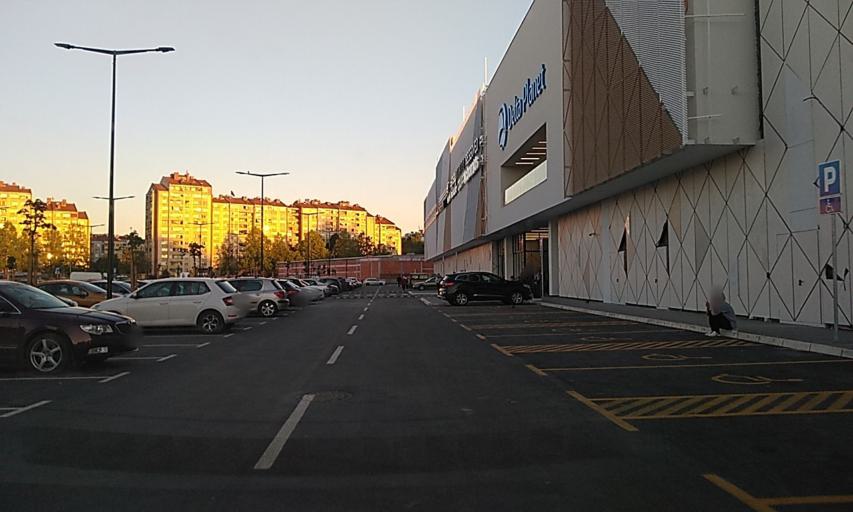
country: RS
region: Central Serbia
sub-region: Nisavski Okrug
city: Nis
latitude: 43.3254
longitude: 21.9113
